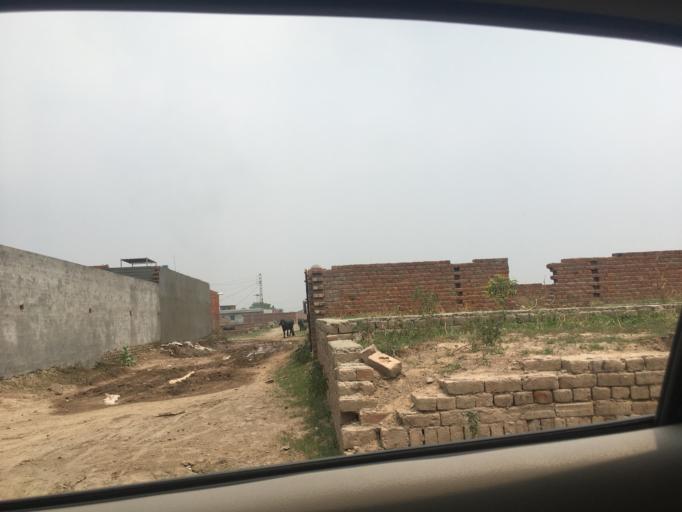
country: PK
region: Punjab
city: Lahore
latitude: 31.6232
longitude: 74.3472
